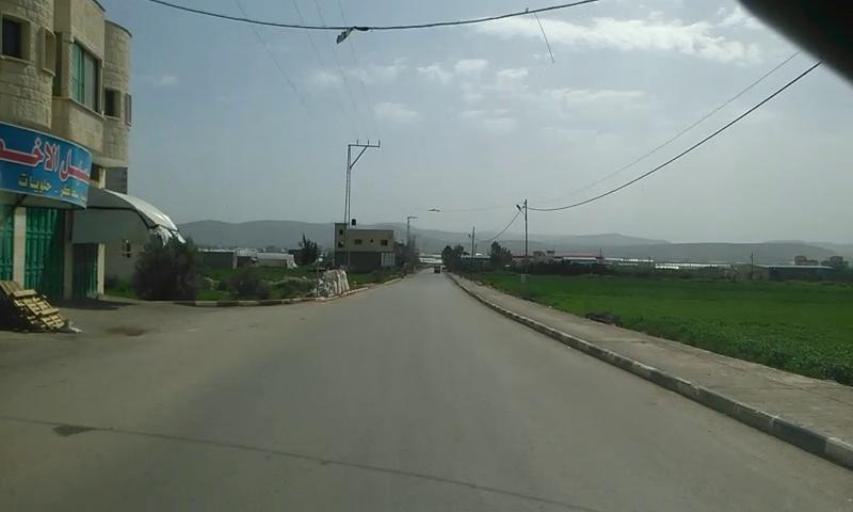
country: PS
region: West Bank
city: Birqin
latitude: 32.4464
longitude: 35.2619
